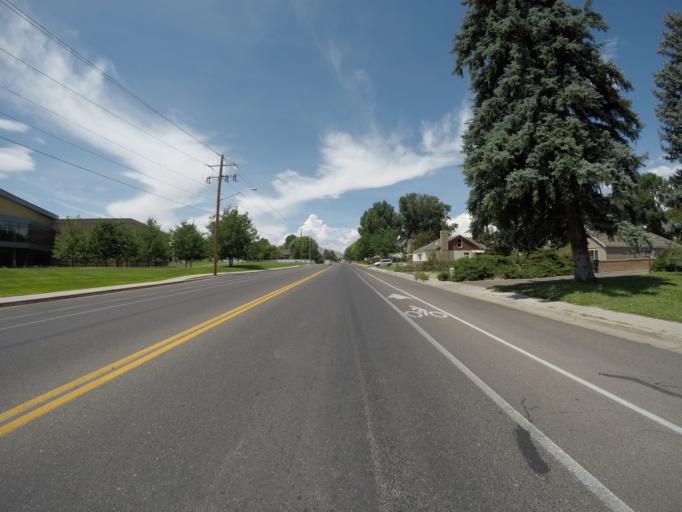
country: US
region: Utah
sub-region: Uintah County
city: Vernal
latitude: 40.4484
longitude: -109.5293
